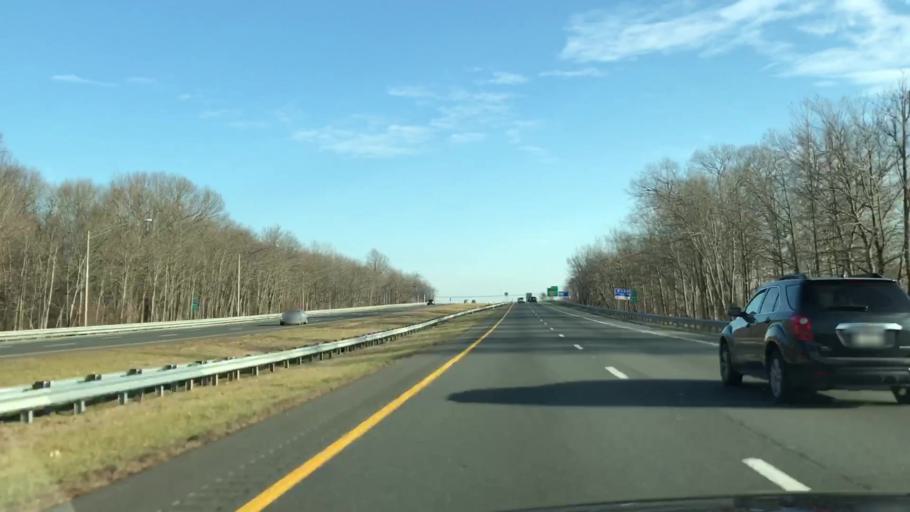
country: US
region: New Jersey
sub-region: Mercer County
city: Robbinsville
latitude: 40.1953
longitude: -74.6061
